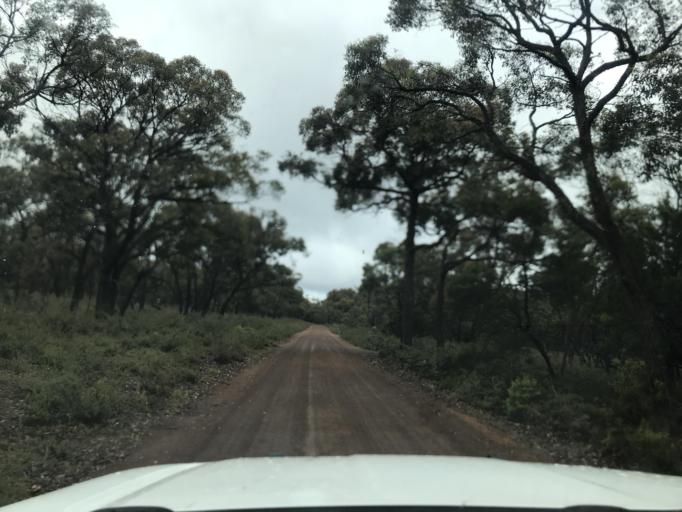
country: AU
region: South Australia
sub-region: Wattle Range
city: Penola
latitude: -37.2600
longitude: 141.3395
